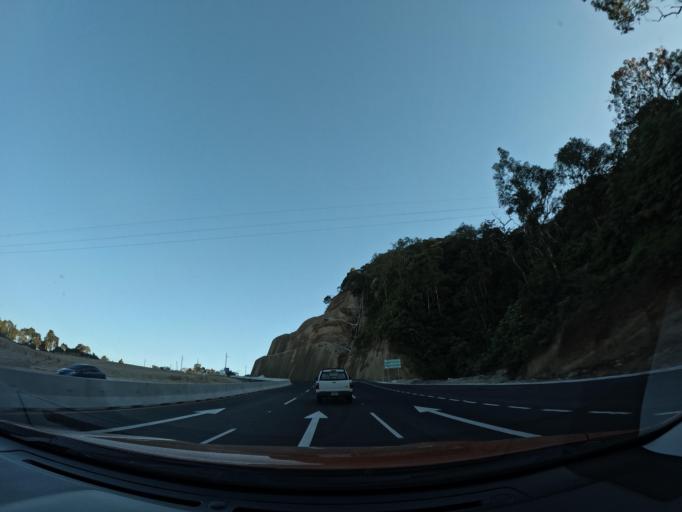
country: GT
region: Guatemala
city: Villa Canales
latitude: 14.4841
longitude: -90.4892
